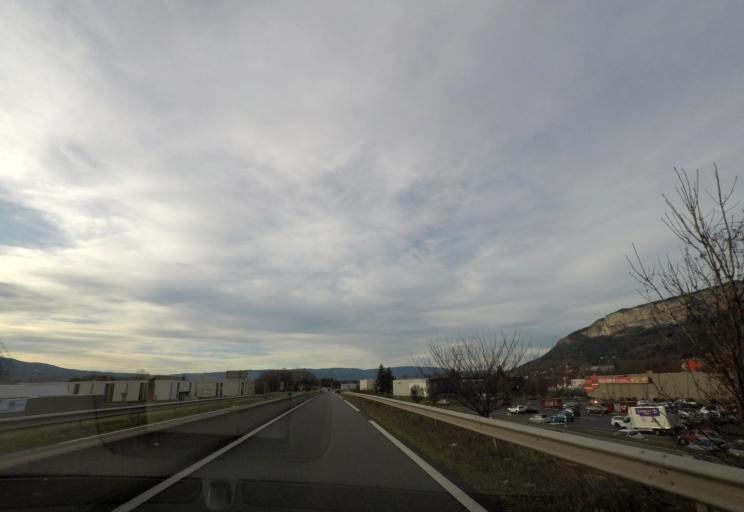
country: FR
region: Rhone-Alpes
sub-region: Departement de la Haute-Savoie
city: Bonneville
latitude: 46.0721
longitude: 6.4198
